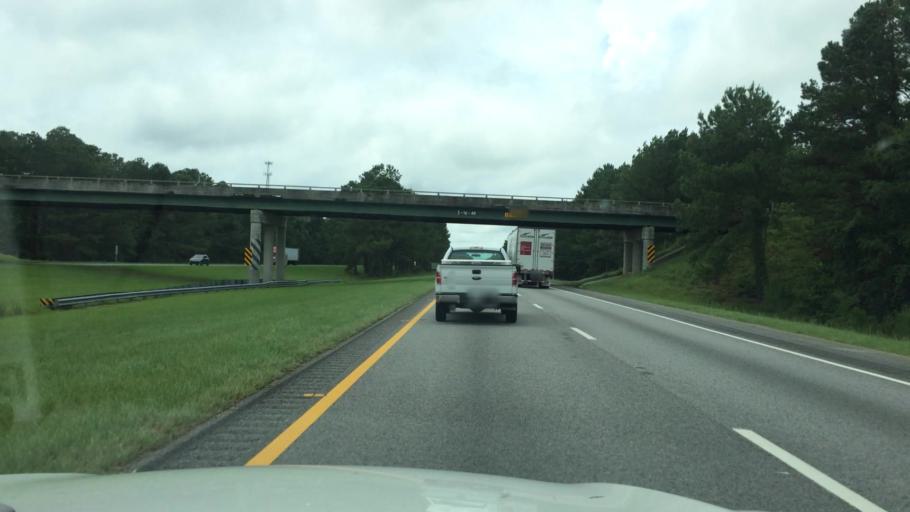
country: US
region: South Carolina
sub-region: Florence County
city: Timmonsville
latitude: 34.2054
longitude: -79.9694
